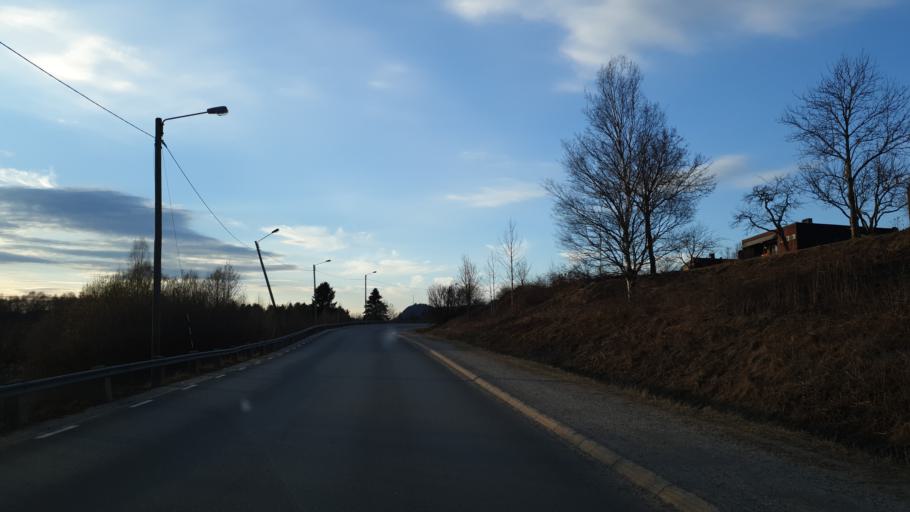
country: SE
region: Vaesternorrland
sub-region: Sundsvalls Kommun
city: Njurundabommen
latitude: 62.2738
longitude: 17.3962
